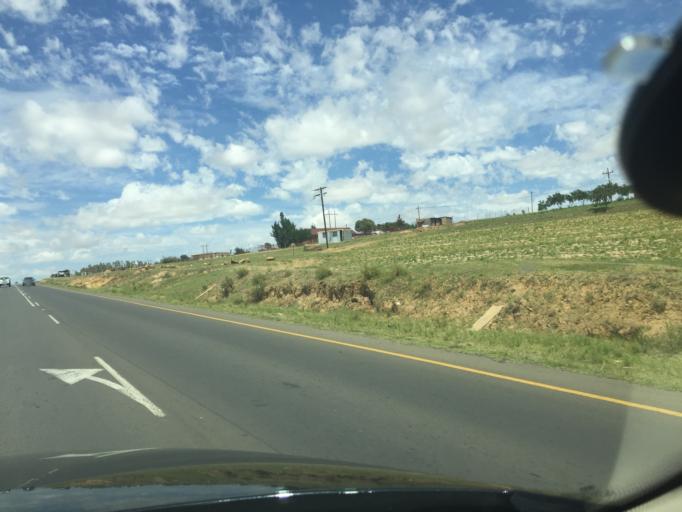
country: LS
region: Mafeteng
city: Mafeteng
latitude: -29.7664
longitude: 27.3155
